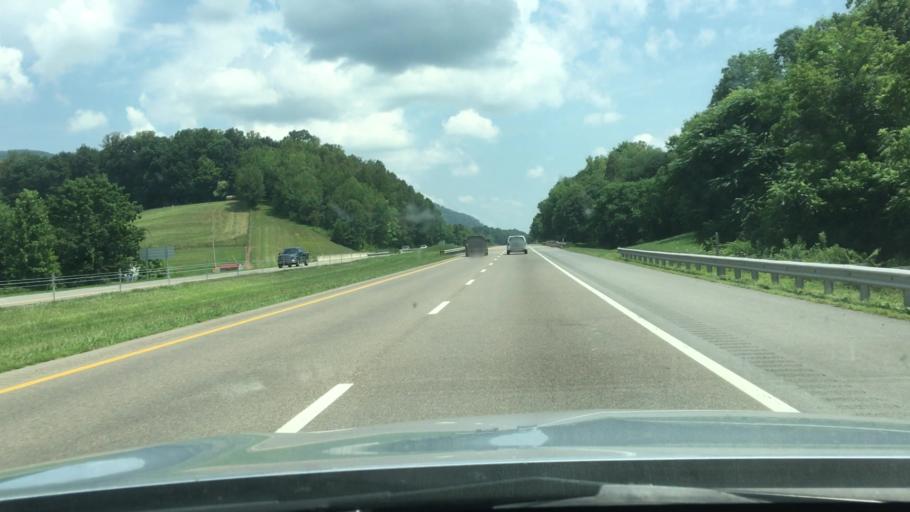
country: US
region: Tennessee
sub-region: Unicoi County
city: Unicoi
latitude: 36.2170
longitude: -82.3446
